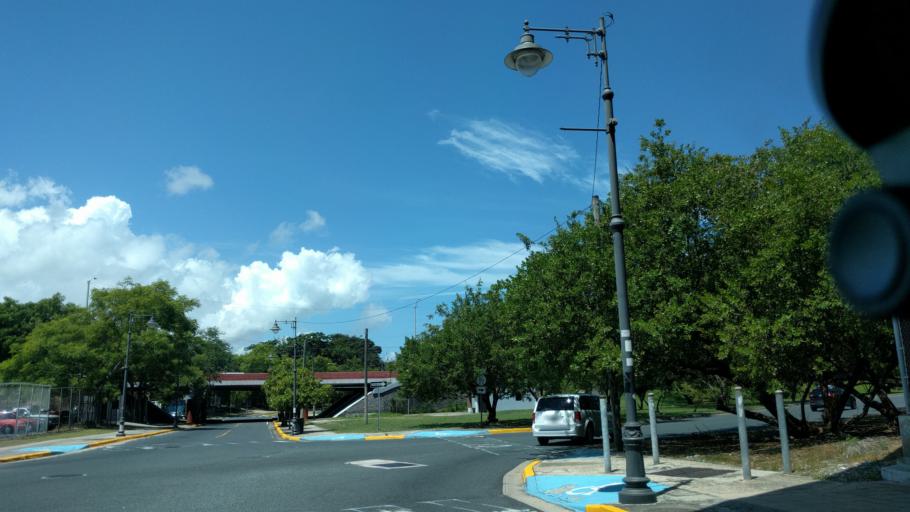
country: PR
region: San Juan
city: San Juan
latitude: 18.4372
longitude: -66.0612
